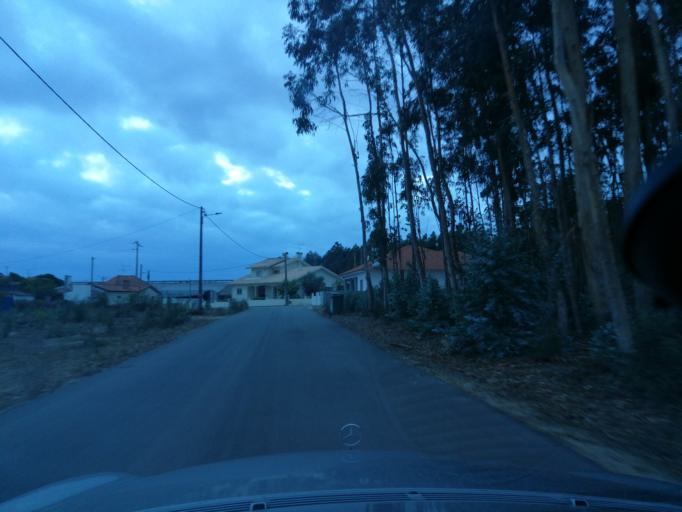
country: PT
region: Aveiro
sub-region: Estarreja
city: Estarreja
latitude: 40.7670
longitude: -8.5939
